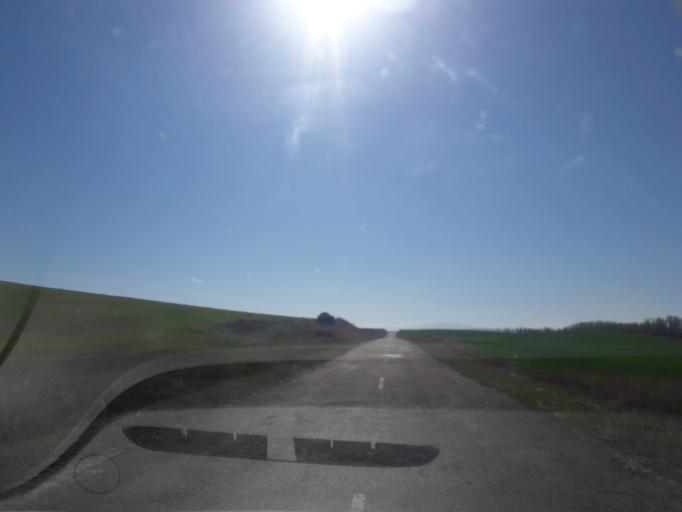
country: ES
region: Castille and Leon
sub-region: Provincia de Salamanca
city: Mancera de Abajo
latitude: 40.8268
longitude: -5.1821
